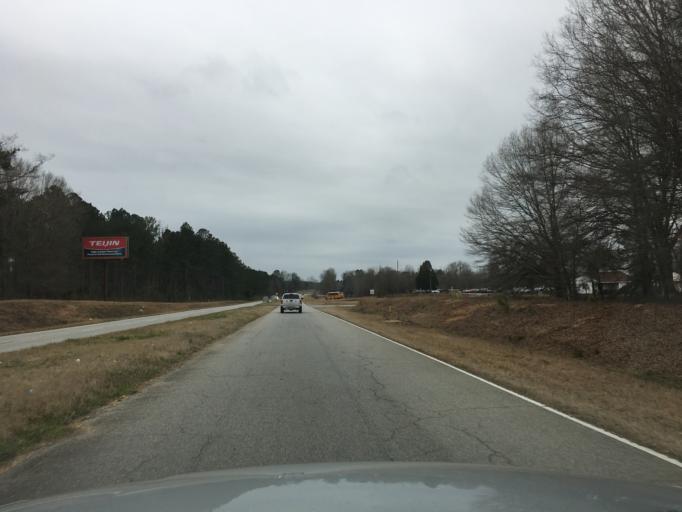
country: US
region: South Carolina
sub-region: Greenwood County
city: Greenwood
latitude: 34.1510
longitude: -82.1406
